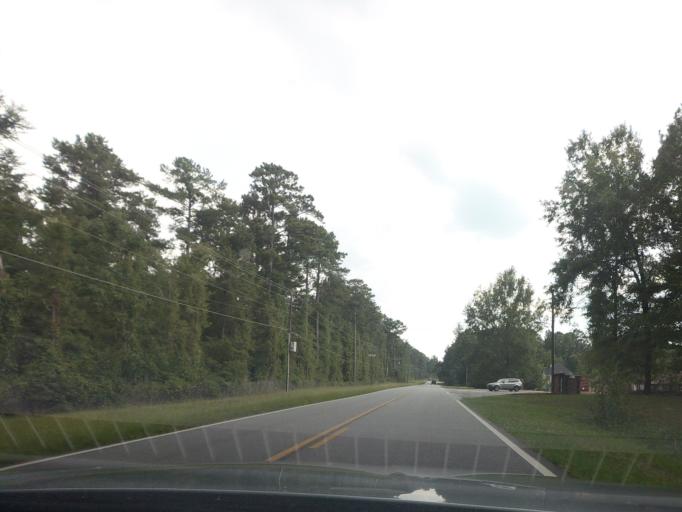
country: US
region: Georgia
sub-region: Bibb County
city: West Point
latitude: 32.8611
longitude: -83.7842
